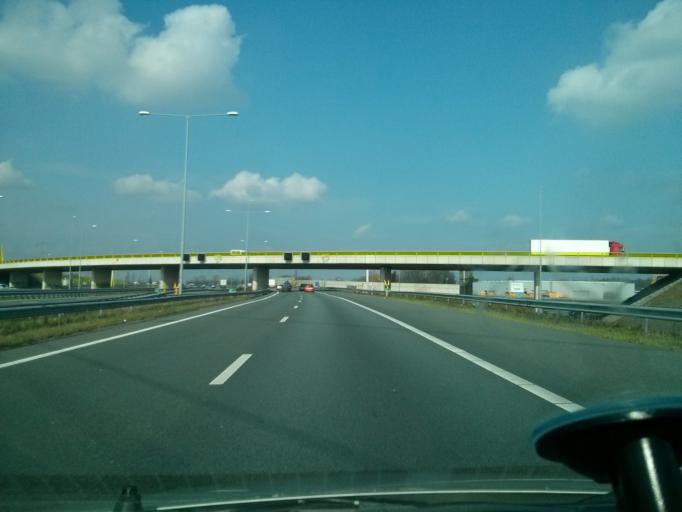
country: NL
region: North Brabant
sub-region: Gemeente 's-Hertogenbosch
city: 's-Hertogenbosch
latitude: 51.6972
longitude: 5.3522
